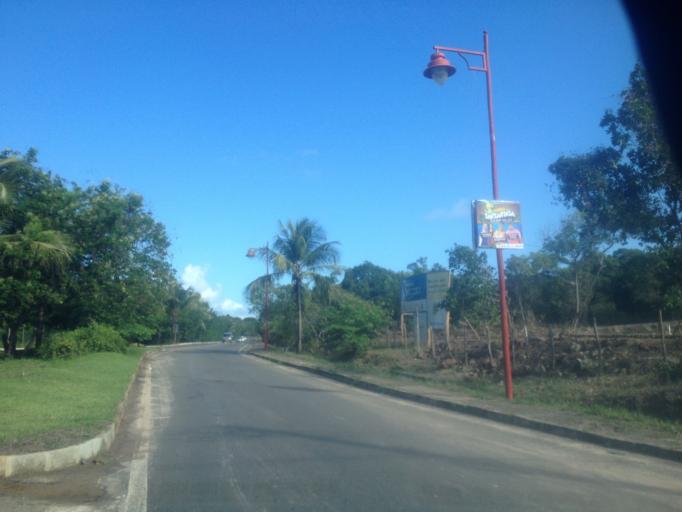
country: BR
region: Bahia
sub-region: Mata De Sao Joao
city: Mata de Sao Joao
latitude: -12.5656
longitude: -38.0173
